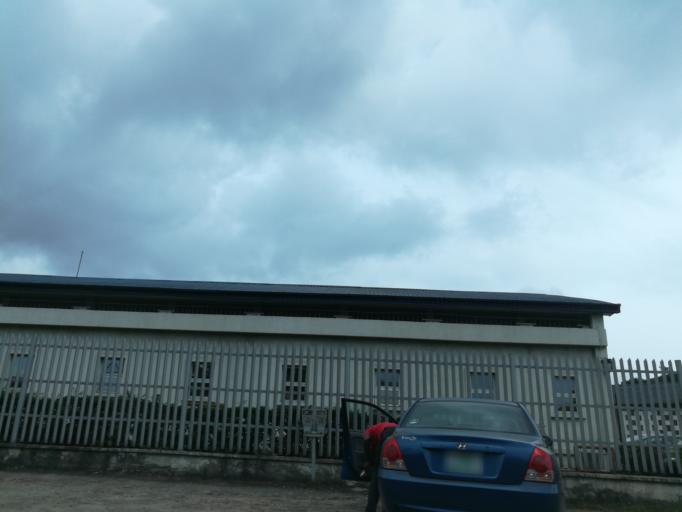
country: NG
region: Lagos
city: Ikeja
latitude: 6.6051
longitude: 3.3377
